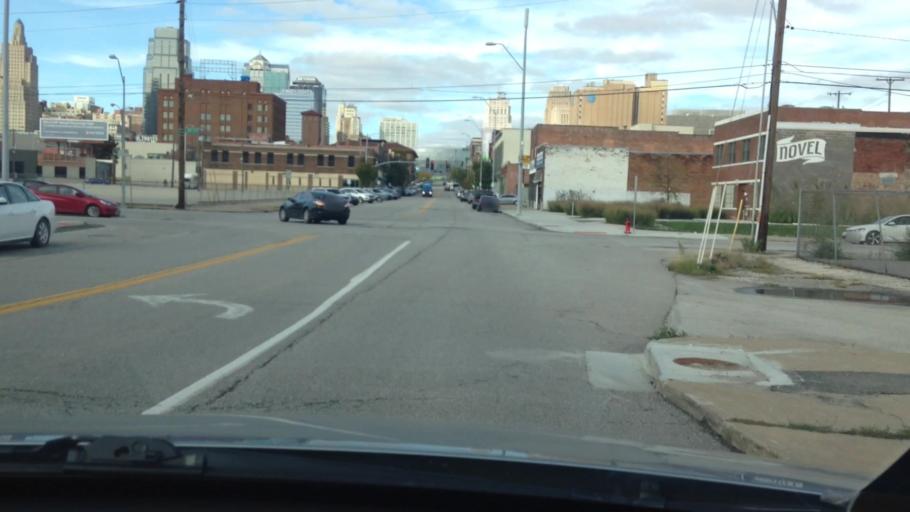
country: US
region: Missouri
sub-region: Jackson County
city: Kansas City
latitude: 39.0886
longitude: -94.5803
